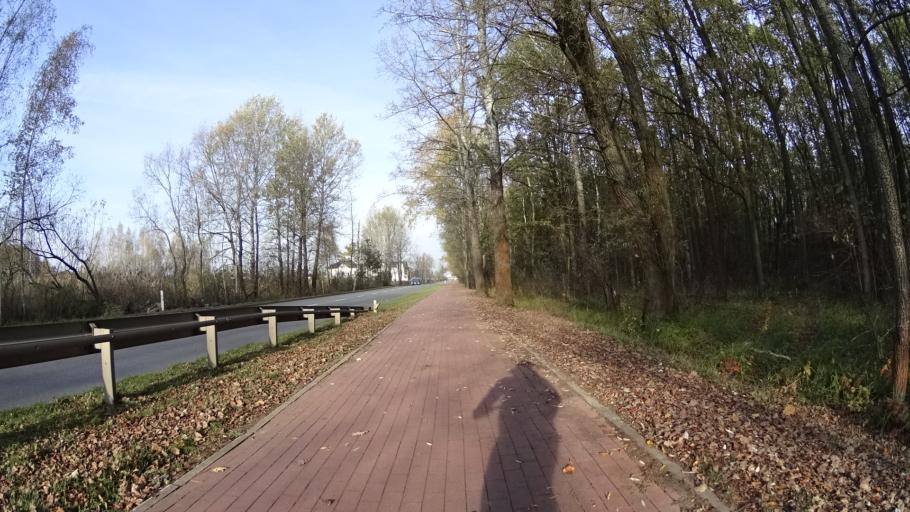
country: PL
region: Masovian Voivodeship
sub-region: Powiat warszawski zachodni
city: Babice
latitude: 52.2707
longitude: 20.8620
